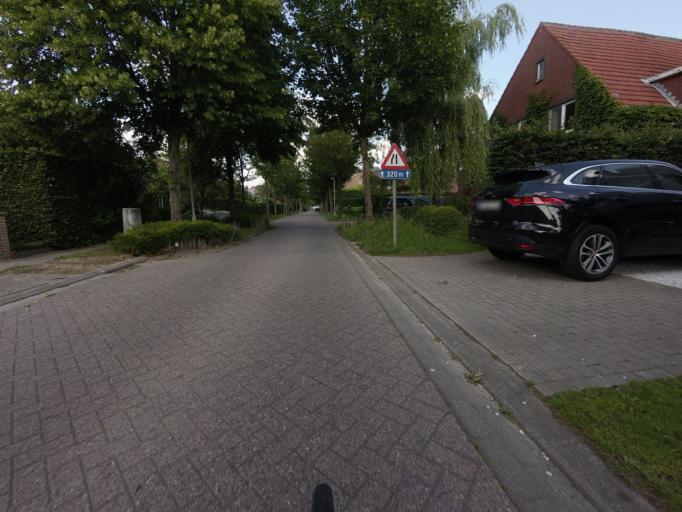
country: BE
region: Flanders
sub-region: Provincie Antwerpen
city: Lint
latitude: 51.1355
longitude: 4.4908
